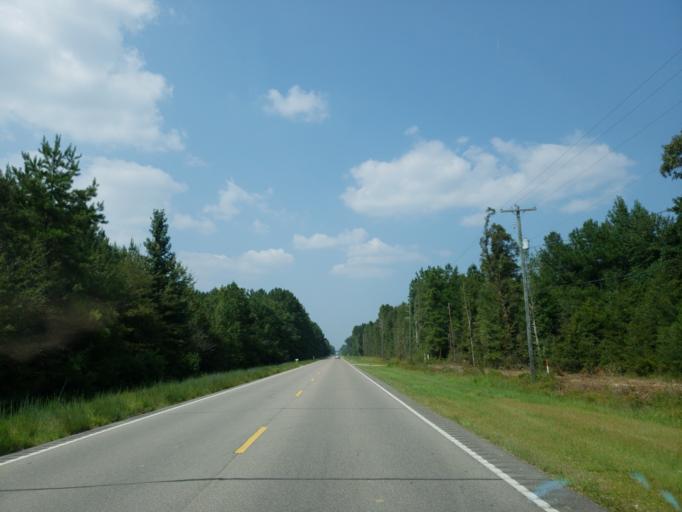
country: US
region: Mississippi
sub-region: Forrest County
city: Glendale
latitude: 31.4572
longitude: -89.2851
